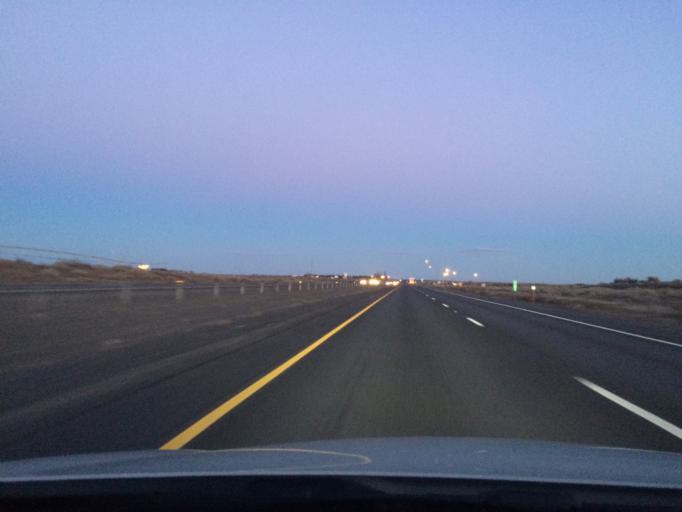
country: US
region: Washington
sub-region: Grant County
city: Royal City
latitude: 47.1038
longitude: -119.6344
